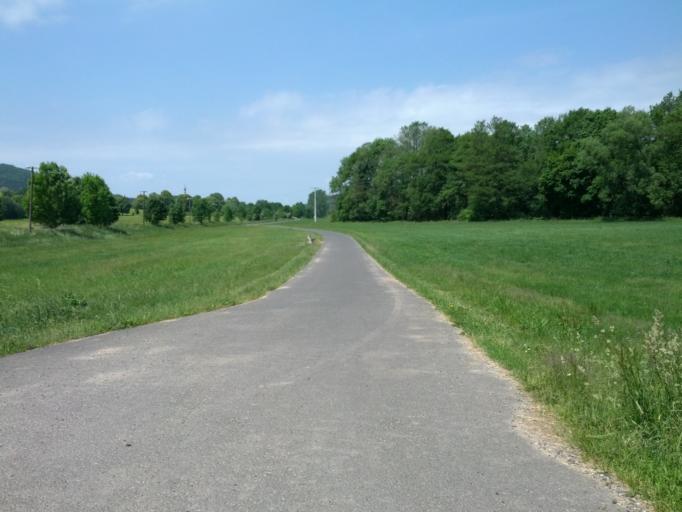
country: DE
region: Thuringia
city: Weilar
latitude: 50.7699
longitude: 10.1415
